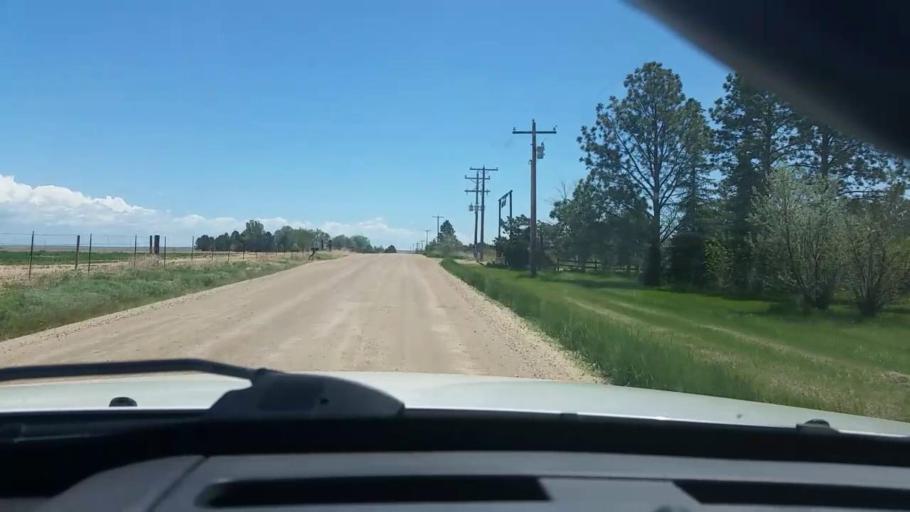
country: US
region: Colorado
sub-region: Larimer County
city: Wellington
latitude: 40.7981
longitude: -105.0639
